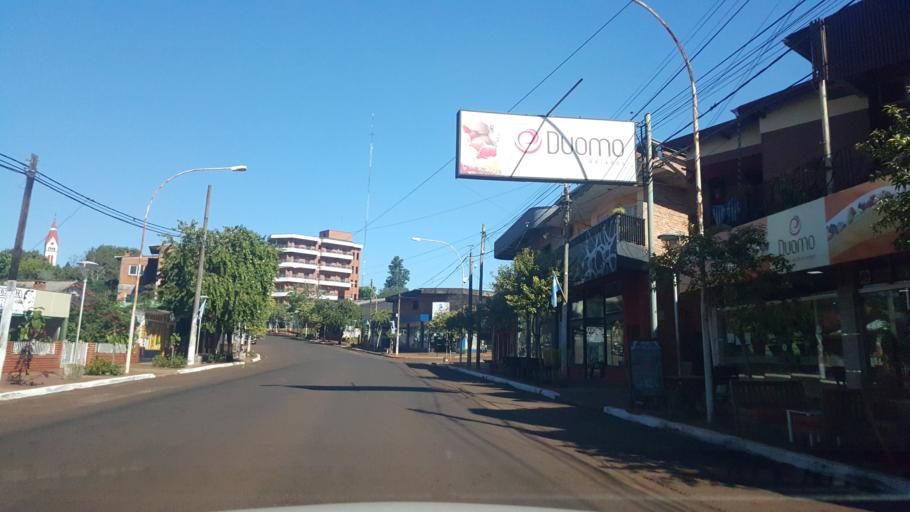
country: AR
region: Misiones
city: Puerto Rico
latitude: -26.8137
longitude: -55.0257
